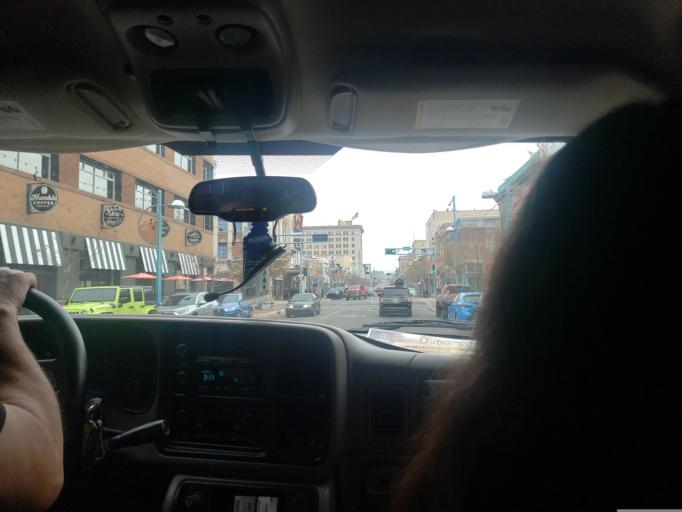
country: US
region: New Mexico
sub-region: Bernalillo County
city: Albuquerque
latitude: 35.0848
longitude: -106.6535
